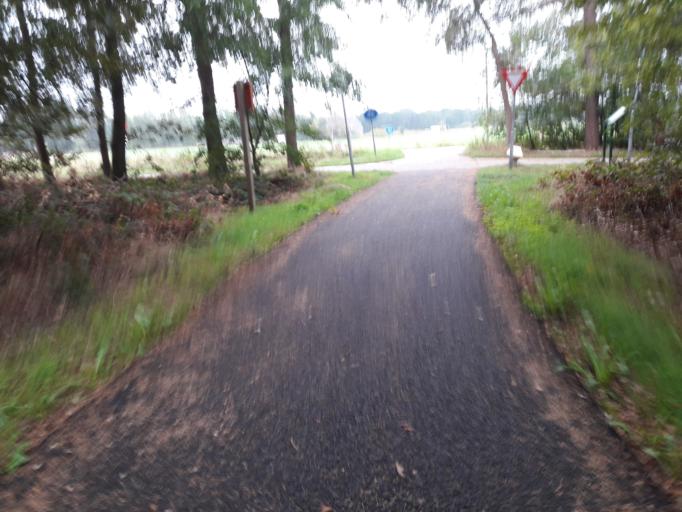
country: NL
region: Drenthe
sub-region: Gemeente Assen
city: Assen
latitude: 52.9004
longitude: 6.5618
